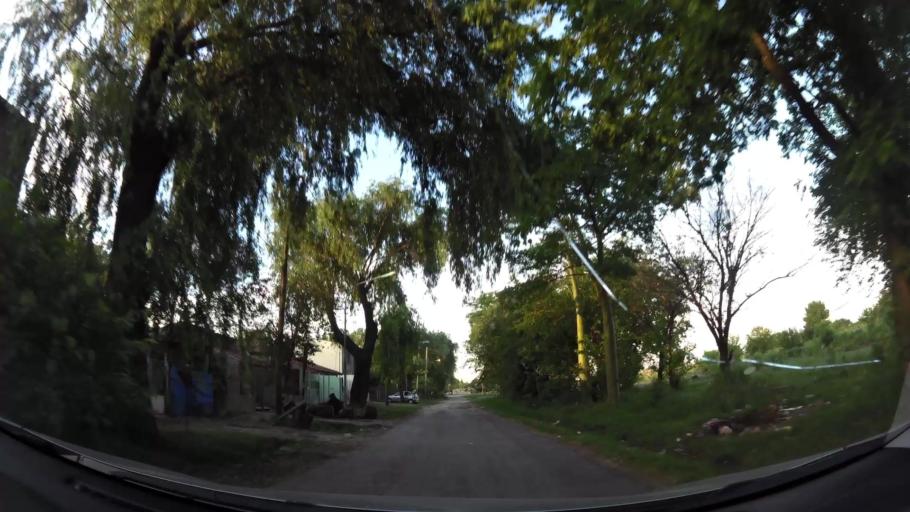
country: AR
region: Buenos Aires
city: Santa Catalina - Dique Lujan
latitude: -34.4421
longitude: -58.6603
